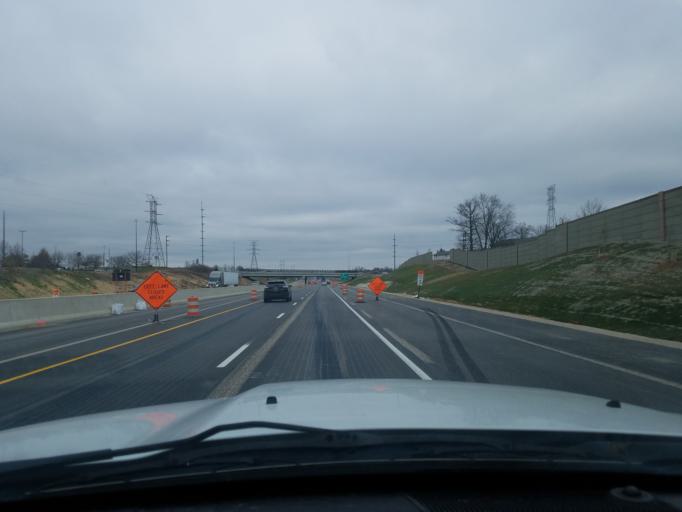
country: US
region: Indiana
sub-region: Monroe County
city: Bloomington
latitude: 39.1442
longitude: -86.5729
